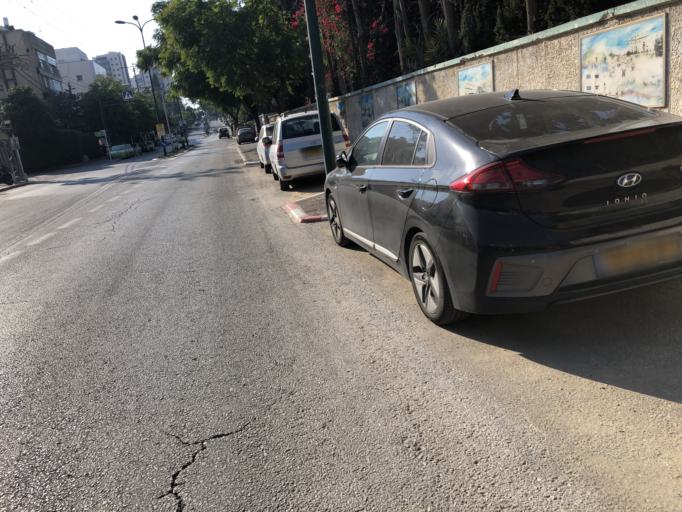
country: IL
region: Tel Aviv
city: Giv`atayim
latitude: 32.0726
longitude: 34.8086
